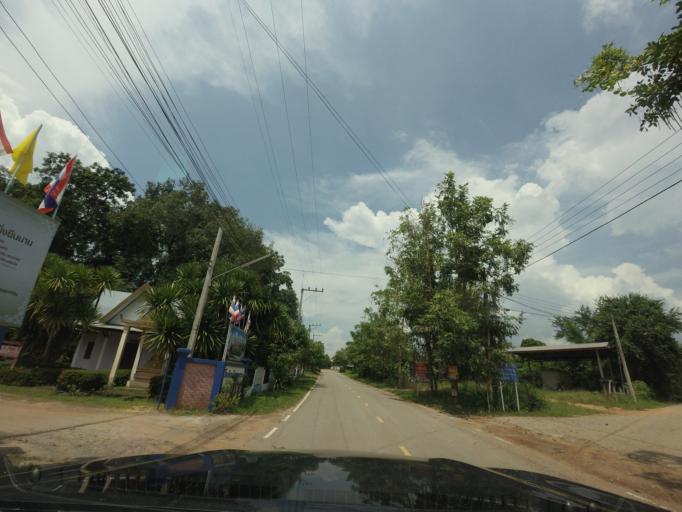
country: TH
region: Khon Kaen
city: Wiang Kao
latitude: 16.6800
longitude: 102.2851
